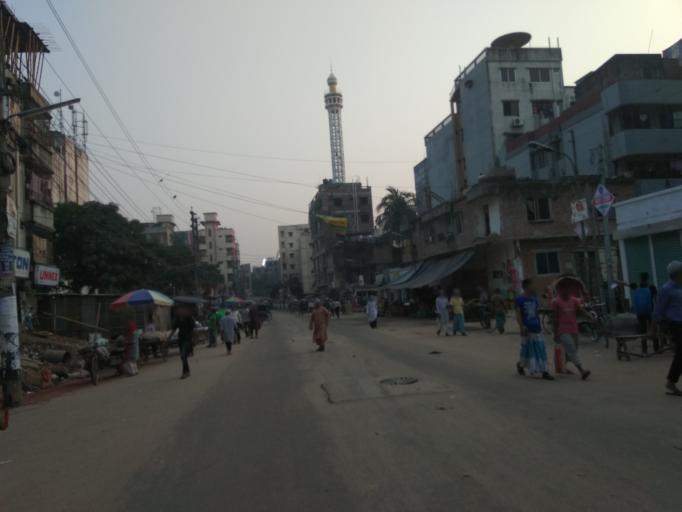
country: BD
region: Dhaka
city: Azimpur
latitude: 23.8121
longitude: 90.3639
